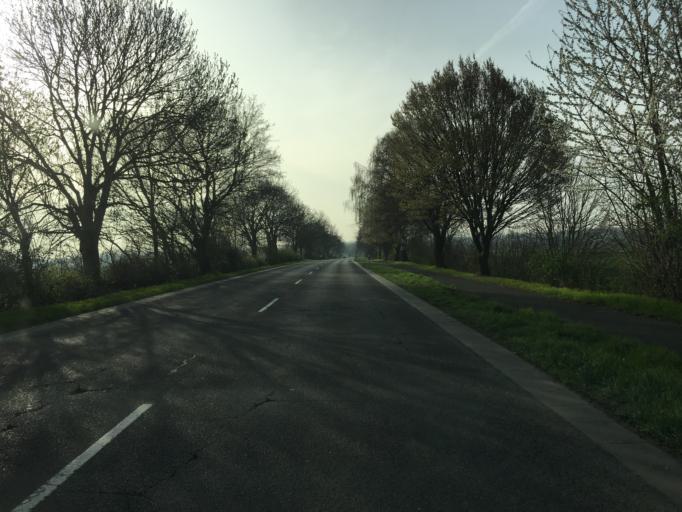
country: DE
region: North Rhine-Westphalia
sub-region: Regierungsbezirk Koln
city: Hurth
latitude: 50.8941
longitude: 6.8505
